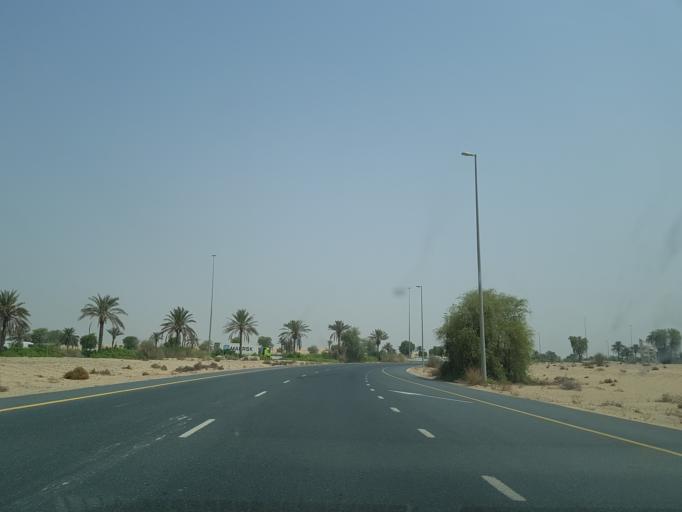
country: AE
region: Dubai
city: Dubai
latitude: 25.0648
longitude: 55.2964
